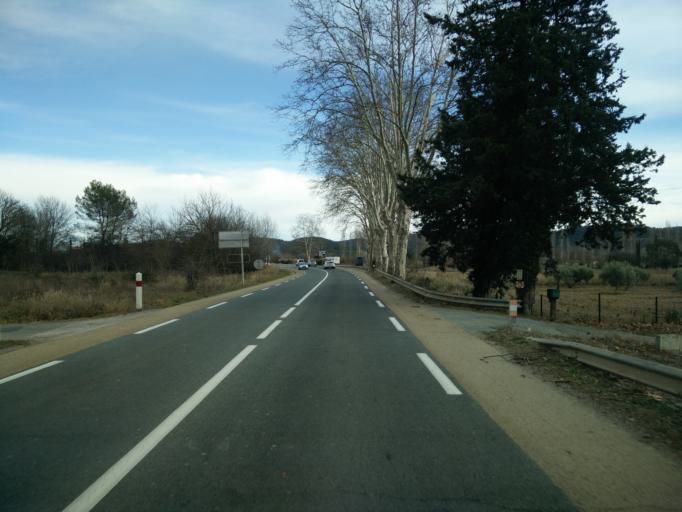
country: FR
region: Provence-Alpes-Cote d'Azur
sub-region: Departement du Var
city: Les Arcs
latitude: 43.4473
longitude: 6.4805
